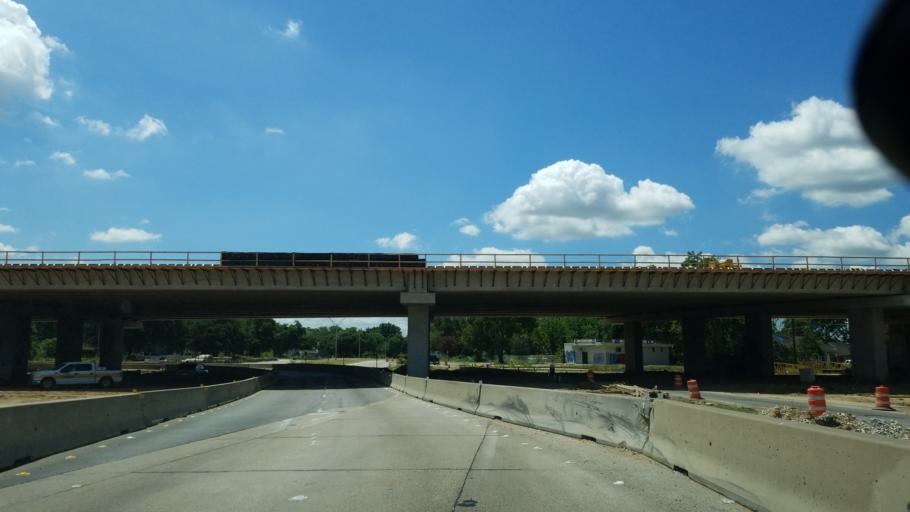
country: US
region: Texas
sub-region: Dallas County
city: Dallas
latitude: 32.7464
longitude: -96.7591
